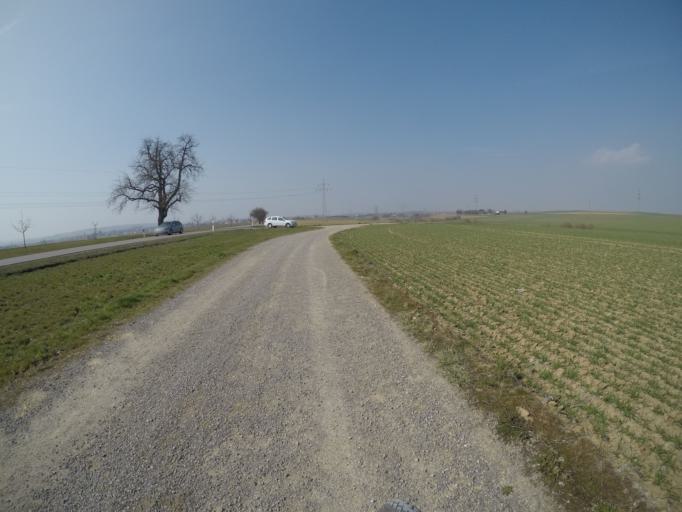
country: DE
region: Baden-Wuerttemberg
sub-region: Regierungsbezirk Stuttgart
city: Herrenberg
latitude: 48.6171
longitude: 8.8648
